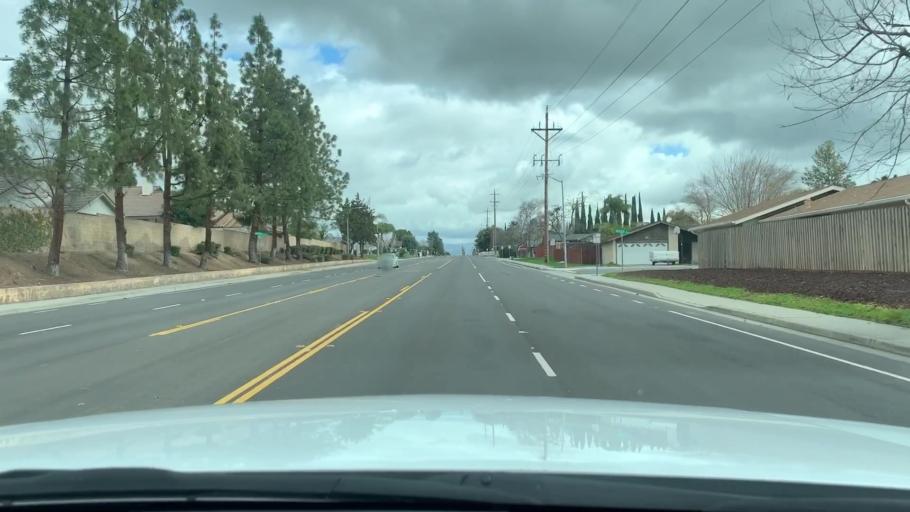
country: US
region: California
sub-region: Kern County
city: Bakersfield
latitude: 35.3978
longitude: -118.9382
